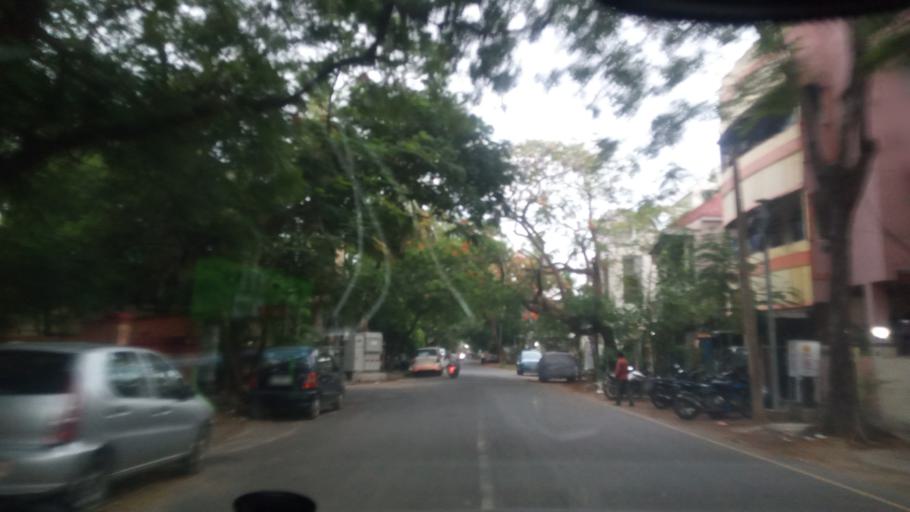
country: IN
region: Tamil Nadu
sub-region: Chennai
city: Chetput
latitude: 13.0402
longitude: 80.2176
